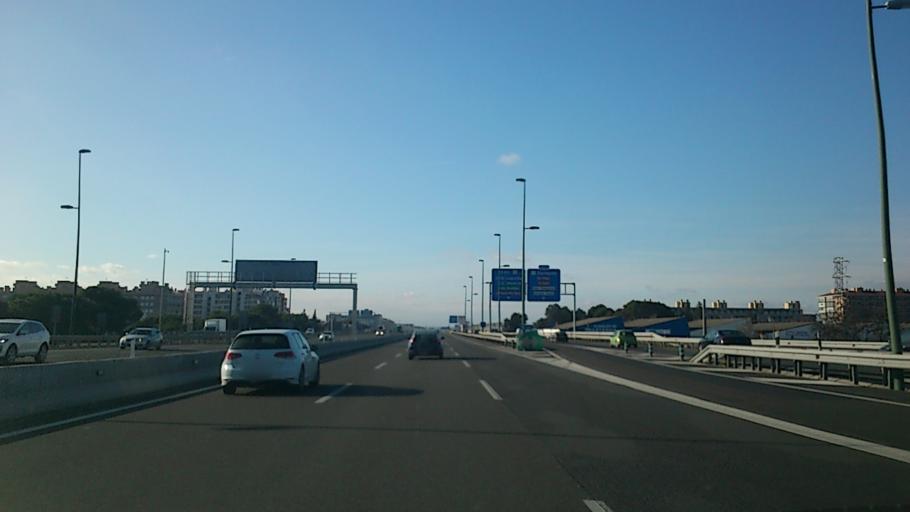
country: ES
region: Aragon
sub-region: Provincia de Zaragoza
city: Zaragoza
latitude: 41.6799
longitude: -0.8656
